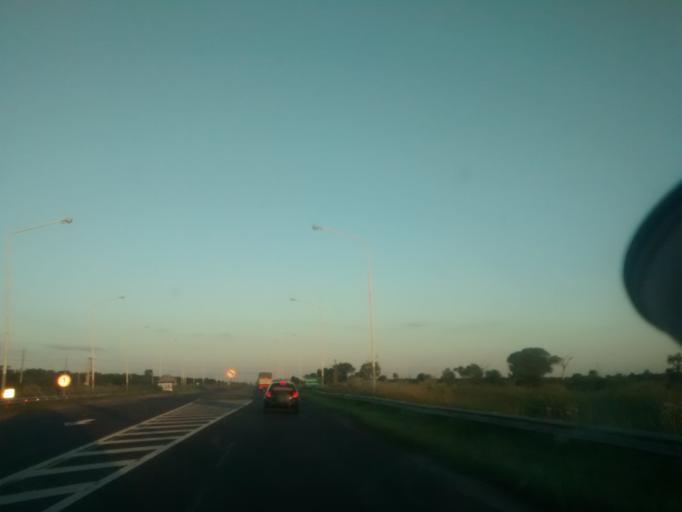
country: AR
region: Chaco
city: La Escondida
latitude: -27.1357
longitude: -59.4666
